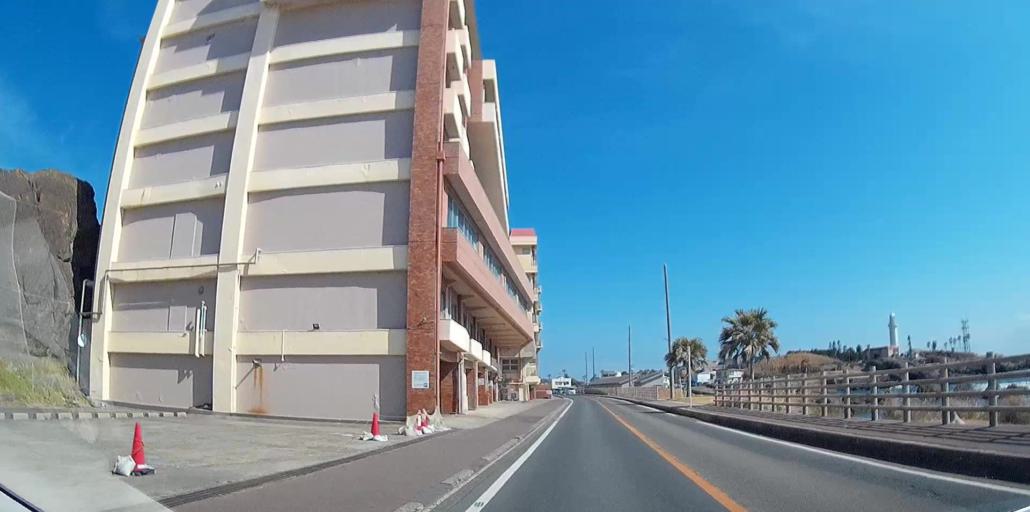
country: JP
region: Chiba
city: Tateyama
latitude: 34.9038
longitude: 139.8853
